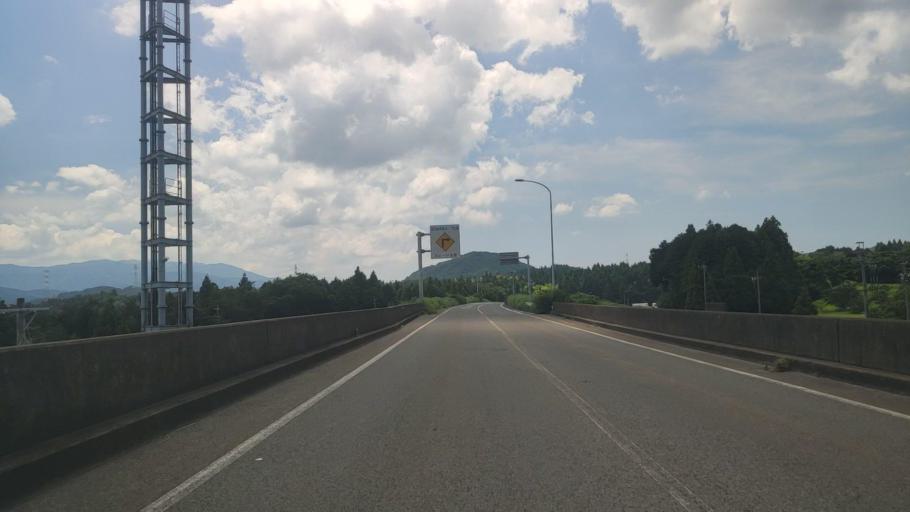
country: JP
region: Gifu
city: Tarui
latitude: 35.3709
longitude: 136.4532
